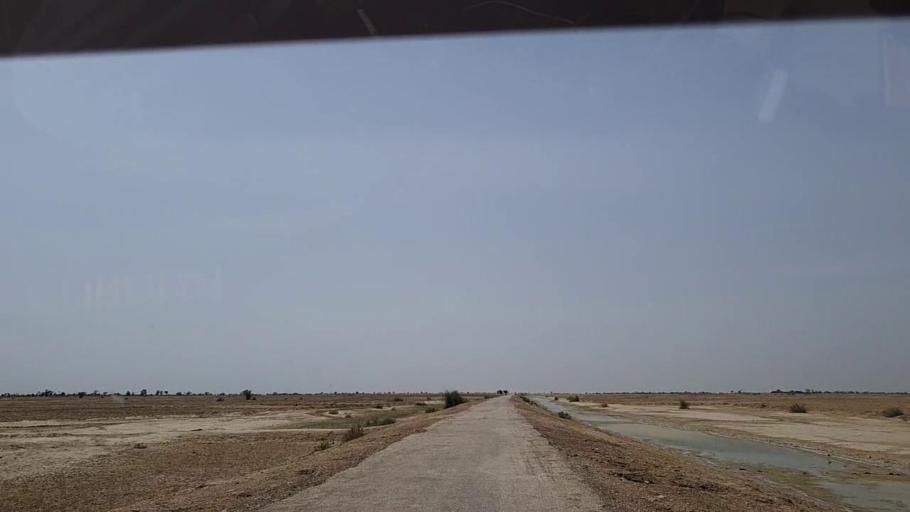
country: PK
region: Sindh
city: Johi
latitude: 26.7240
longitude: 67.6430
